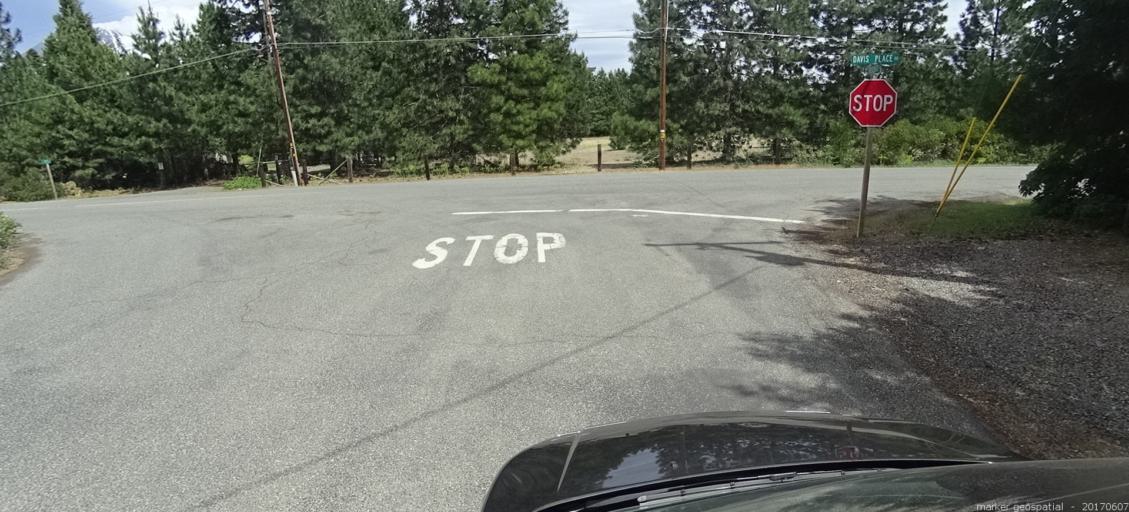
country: US
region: California
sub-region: Siskiyou County
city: Mount Shasta
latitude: 41.3373
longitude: -122.3685
